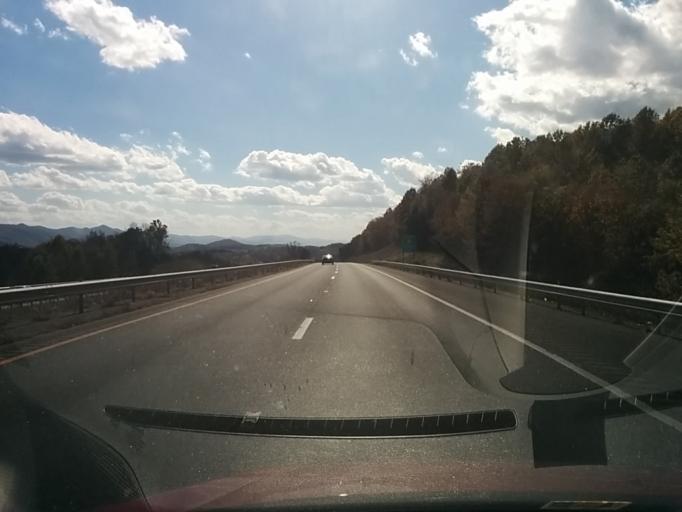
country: US
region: Virginia
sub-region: City of Buena Vista
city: Buena Vista
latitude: 37.8971
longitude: -79.2729
